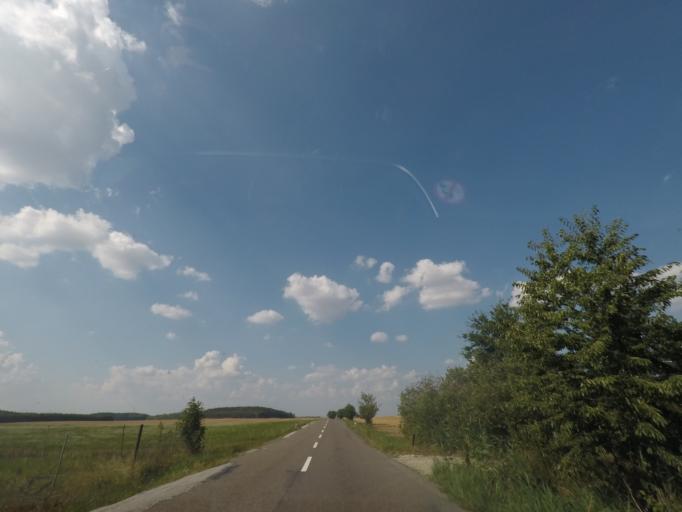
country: CZ
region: Kralovehradecky
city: Dolni Cernilov
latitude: 50.2439
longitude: 15.9646
